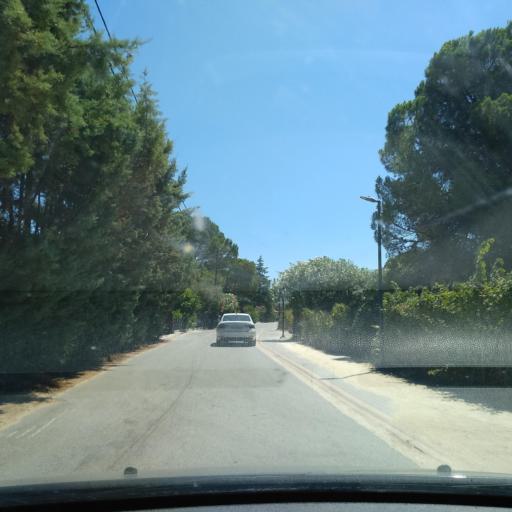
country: GR
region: Central Macedonia
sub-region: Nomos Chalkidikis
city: Neos Marmaras
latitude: 40.1876
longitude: 23.7851
